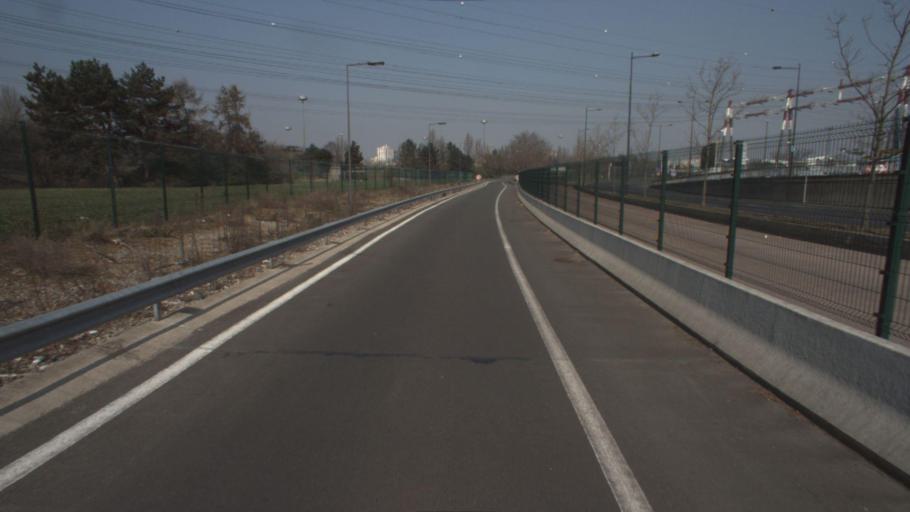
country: FR
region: Ile-de-France
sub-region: Departement du Val-de-Marne
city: Chevilly-Larue
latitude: 48.7630
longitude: 2.3449
